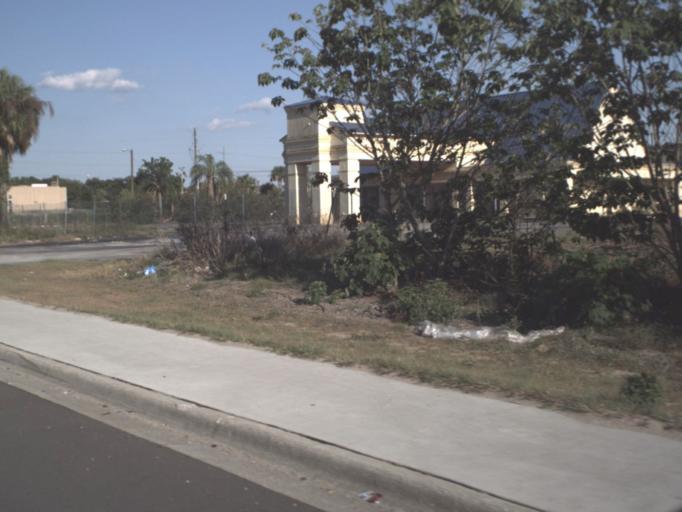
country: US
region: Florida
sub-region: Marion County
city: Ocala
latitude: 29.1863
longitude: -82.1893
